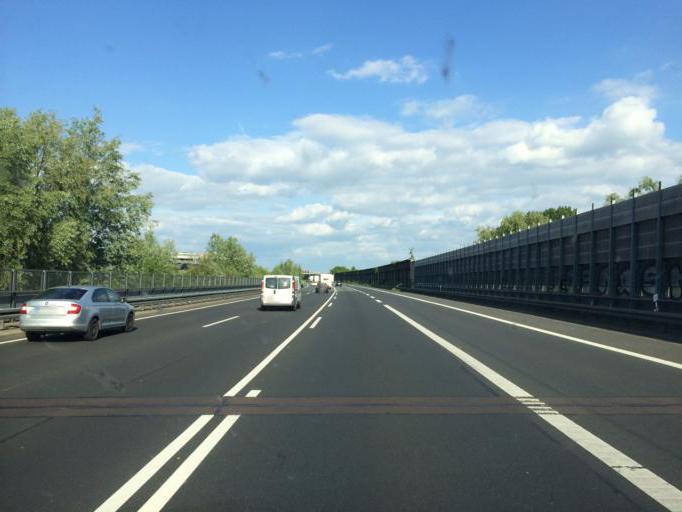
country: DE
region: Lower Saxony
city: Braunschweig
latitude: 52.3133
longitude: 10.5257
